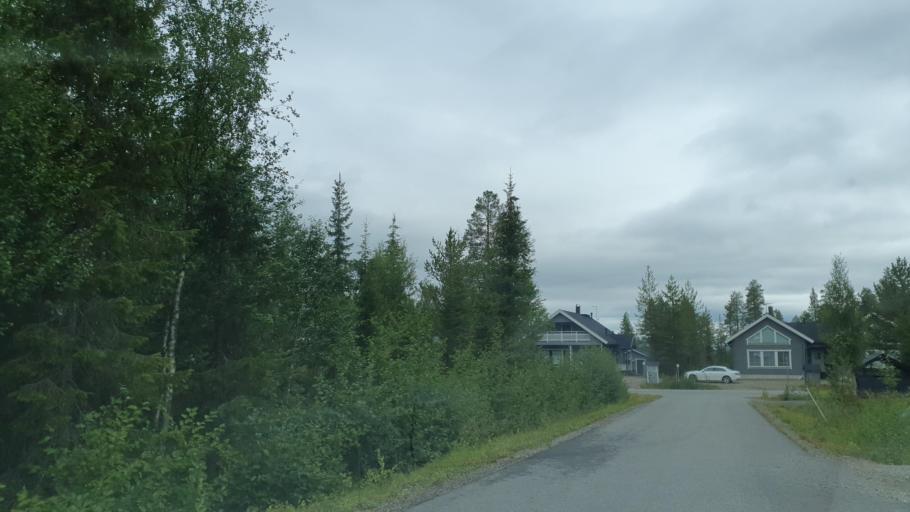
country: FI
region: Lapland
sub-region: Tunturi-Lappi
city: Kolari
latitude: 67.5935
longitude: 24.1727
